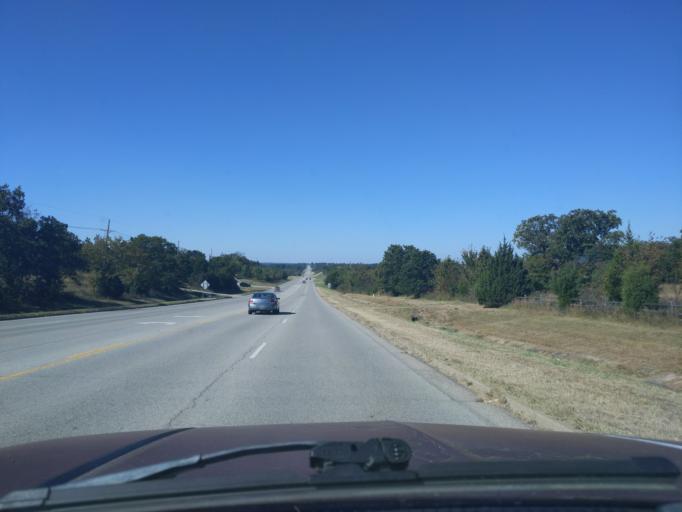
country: US
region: Oklahoma
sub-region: Creek County
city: Kiefer
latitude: 35.9885
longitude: -96.0487
